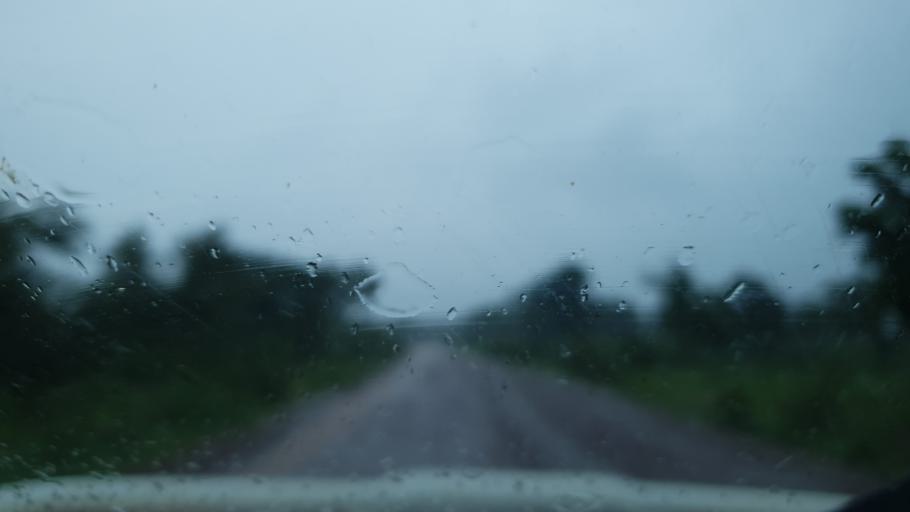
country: ML
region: Sikasso
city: Kolondieba
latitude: 11.6149
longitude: -6.6769
